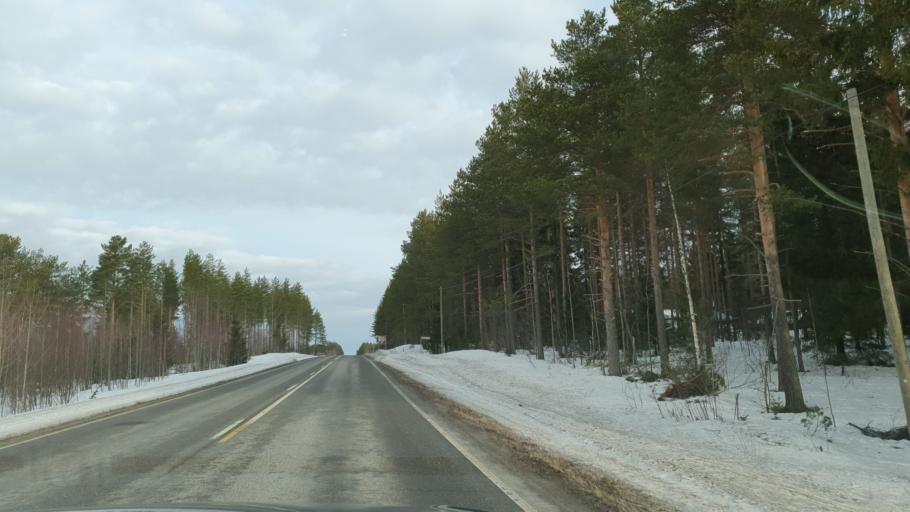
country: FI
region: Kainuu
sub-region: Kajaani
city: Vuokatti
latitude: 64.1793
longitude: 28.1934
